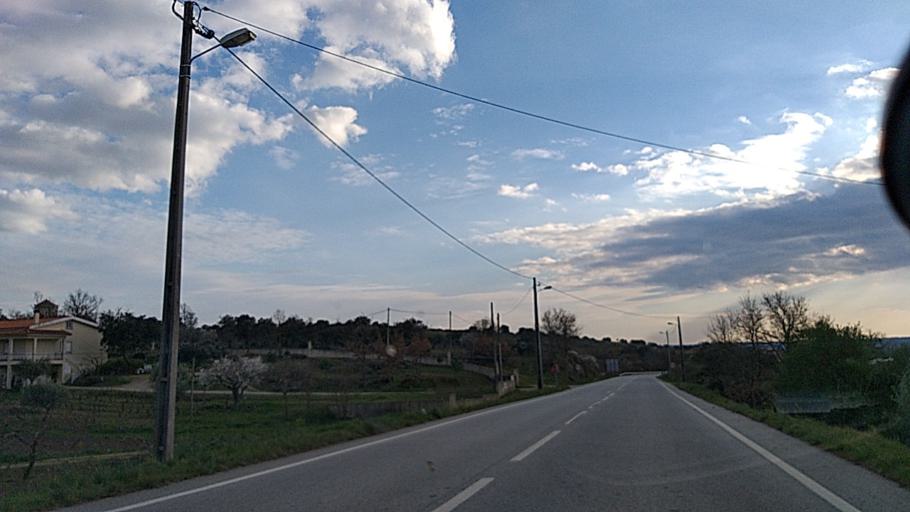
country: ES
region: Castille and Leon
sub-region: Provincia de Salamanca
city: Aldea del Obispo
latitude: 40.7170
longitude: -6.9066
